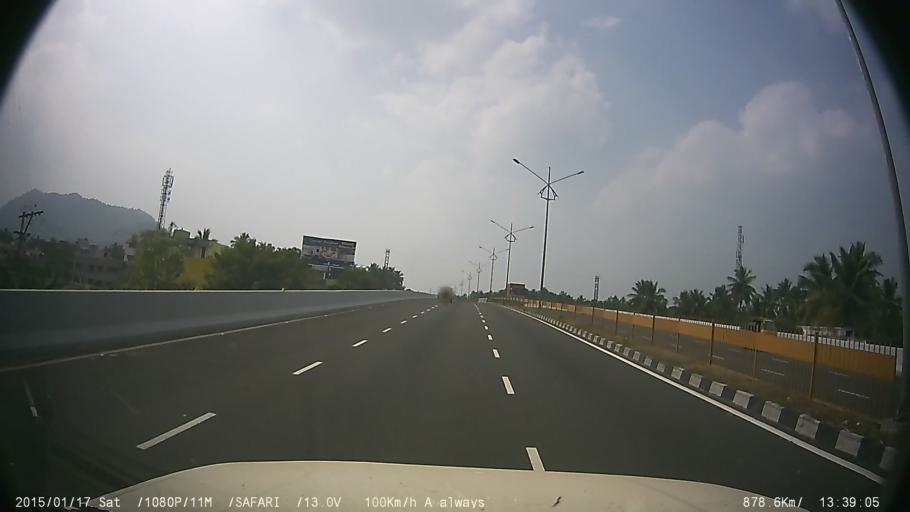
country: IN
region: Tamil Nadu
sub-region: Vellore
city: Katpadi
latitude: 12.9422
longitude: 79.1876
